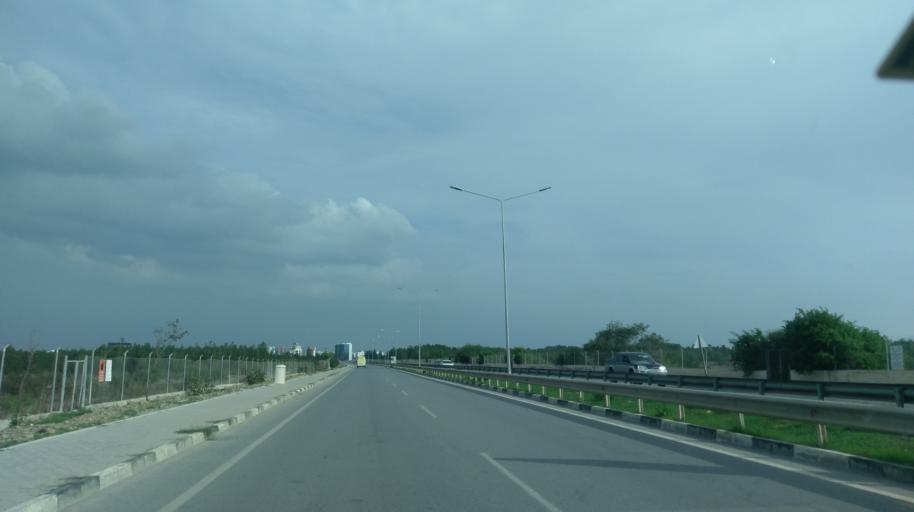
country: CY
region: Lefkosia
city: Nicosia
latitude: 35.1902
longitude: 33.3299
